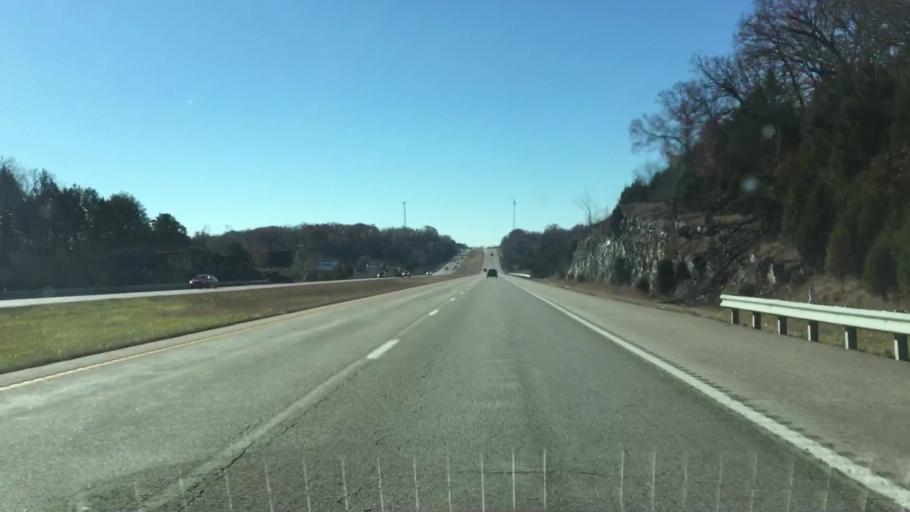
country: US
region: Missouri
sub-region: Cole County
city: Wardsville
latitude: 38.4938
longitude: -92.2694
